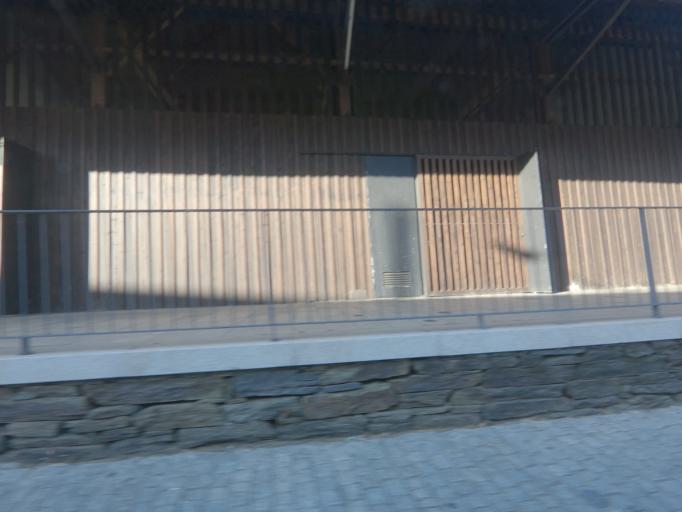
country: PT
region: Vila Real
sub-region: Peso da Regua
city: Peso da Regua
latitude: 41.1571
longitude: -7.7822
